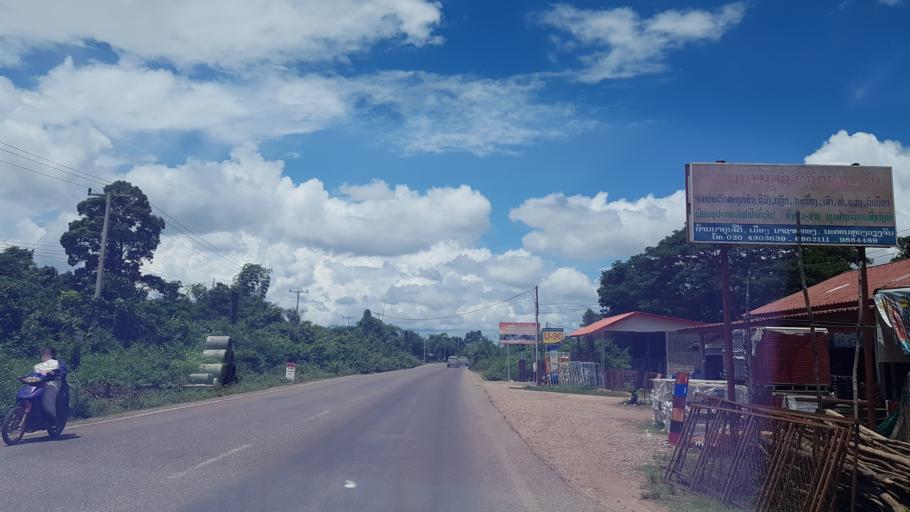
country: LA
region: Vientiane
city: Vientiane
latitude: 18.1101
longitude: 102.5835
